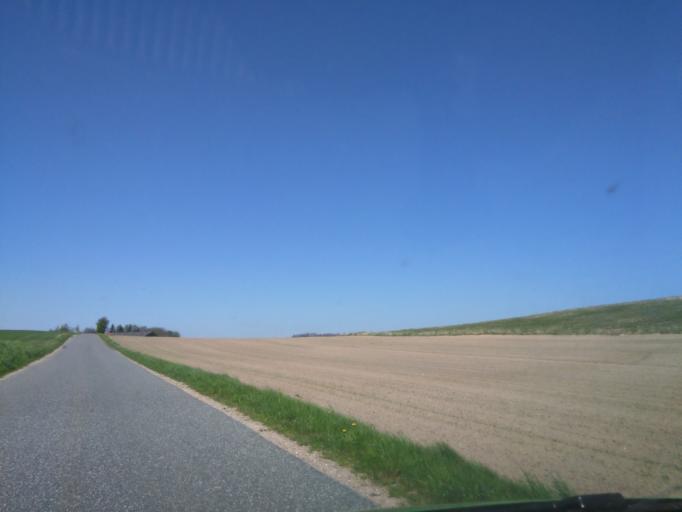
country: DK
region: Central Jutland
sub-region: Odder Kommune
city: Odder
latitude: 55.9011
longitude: 10.0482
